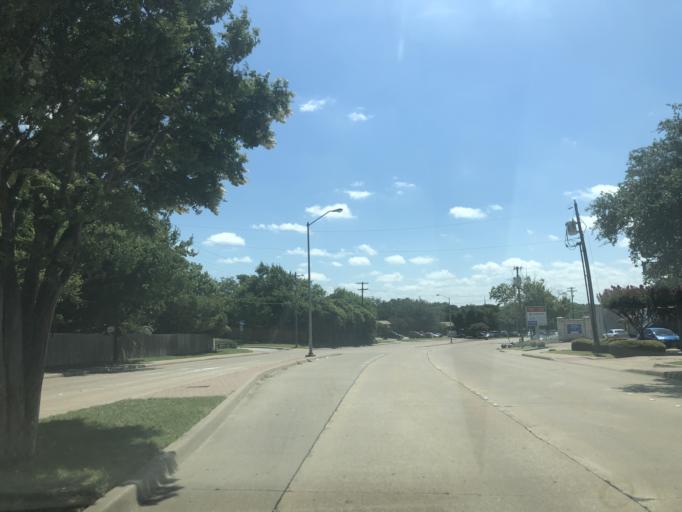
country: US
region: Texas
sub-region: Dallas County
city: Duncanville
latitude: 32.6474
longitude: -96.9216
